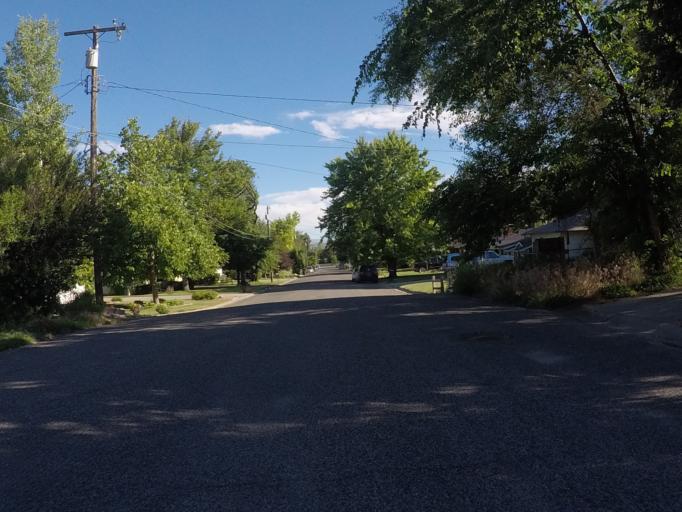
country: US
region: Montana
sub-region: Yellowstone County
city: Billings
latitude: 45.7943
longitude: -108.5846
